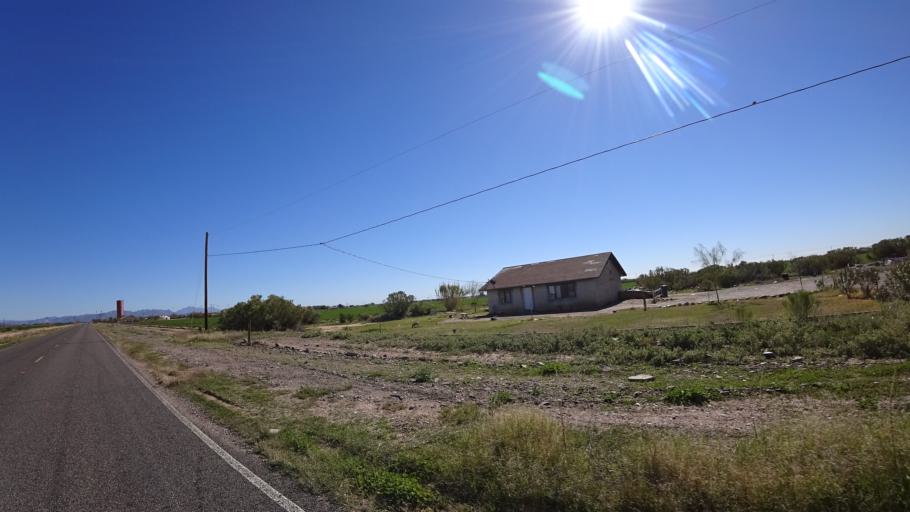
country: US
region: Arizona
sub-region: Maricopa County
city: Scottsdale
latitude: 33.5096
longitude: -111.8454
